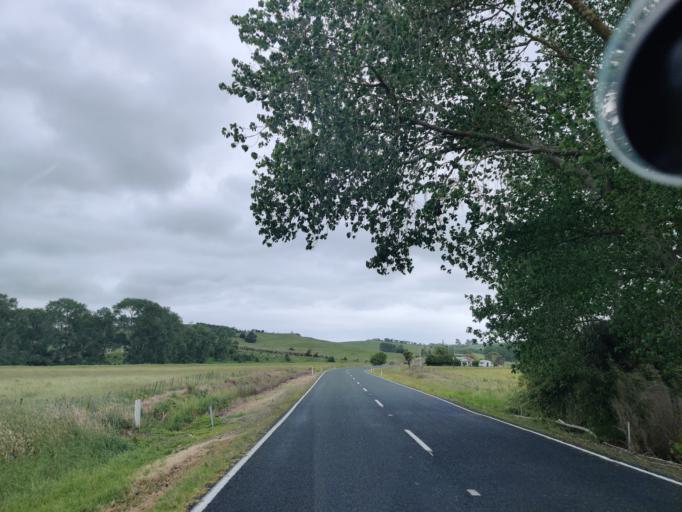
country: NZ
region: Northland
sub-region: Kaipara District
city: Dargaville
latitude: -36.1202
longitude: 174.1045
